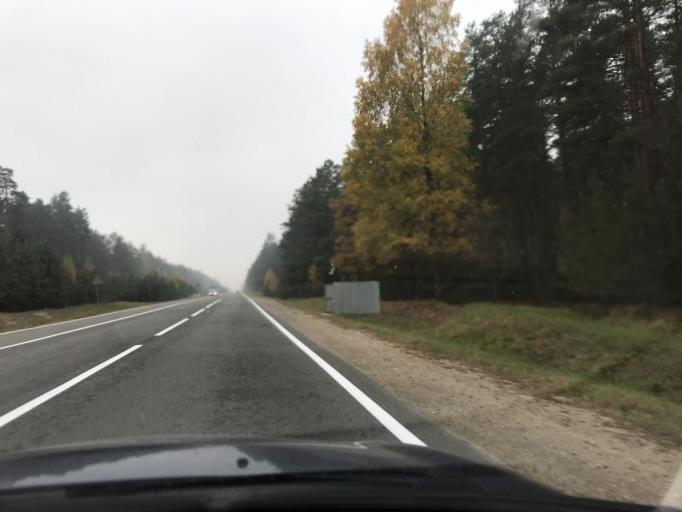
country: LT
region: Alytaus apskritis
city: Druskininkai
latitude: 53.9170
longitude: 23.9242
